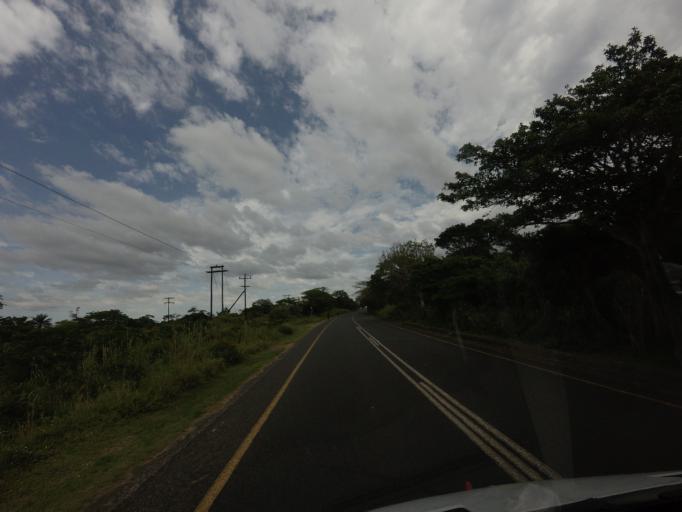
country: ZA
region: KwaZulu-Natal
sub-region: uMkhanyakude District Municipality
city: Mtubatuba
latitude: -28.3735
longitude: 32.3970
